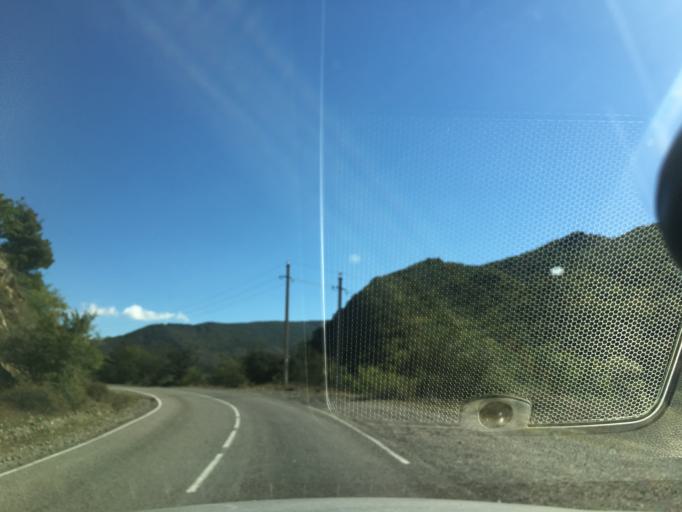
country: GE
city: Zahesi
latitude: 41.8270
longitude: 44.8422
